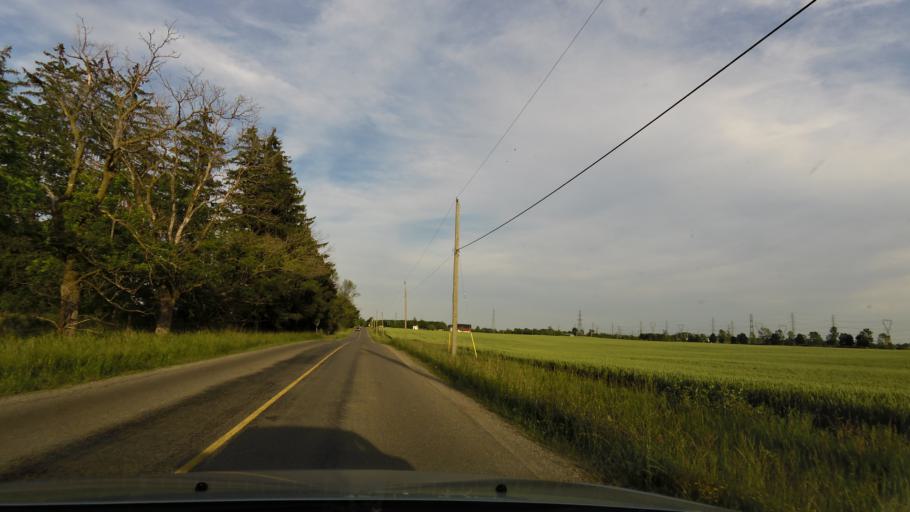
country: CA
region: Ontario
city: Ancaster
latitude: 43.0579
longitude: -79.9767
